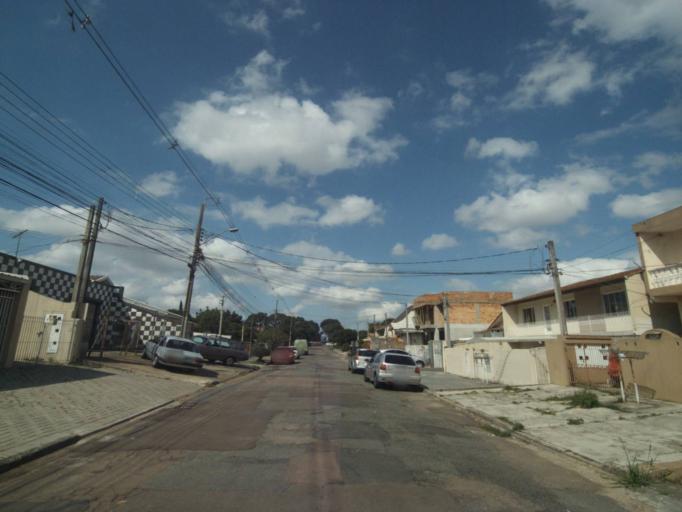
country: BR
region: Parana
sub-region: Curitiba
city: Curitiba
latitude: -25.5011
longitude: -49.3142
